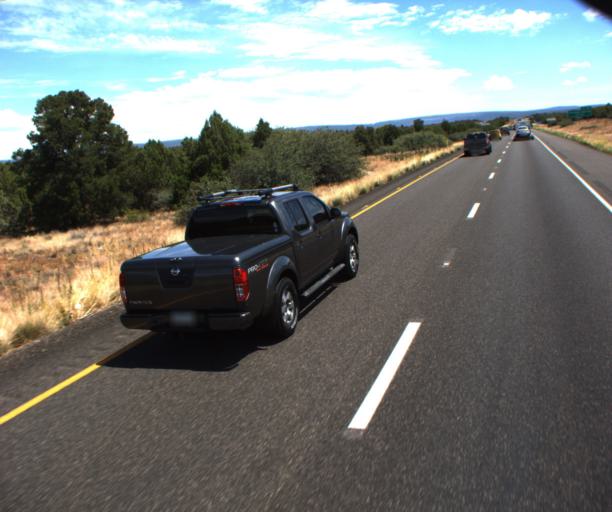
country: US
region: Arizona
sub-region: Yavapai County
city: Village of Oak Creek (Big Park)
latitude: 34.7461
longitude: -111.6822
